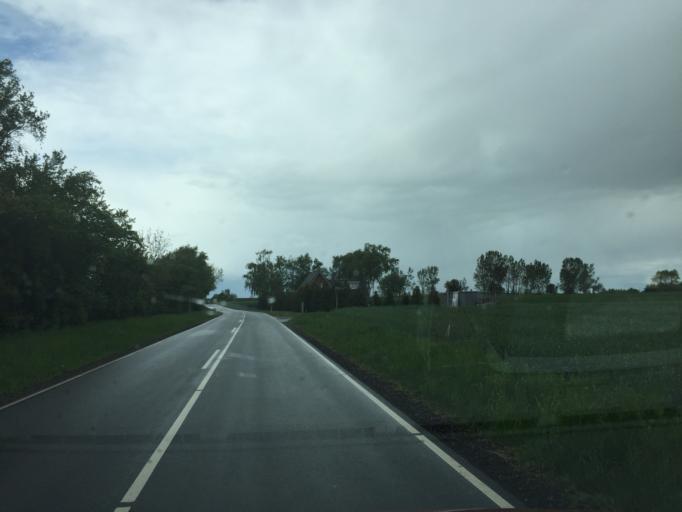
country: DK
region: South Denmark
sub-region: Nordfyns Kommune
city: Bogense
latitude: 55.5298
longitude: 10.0988
